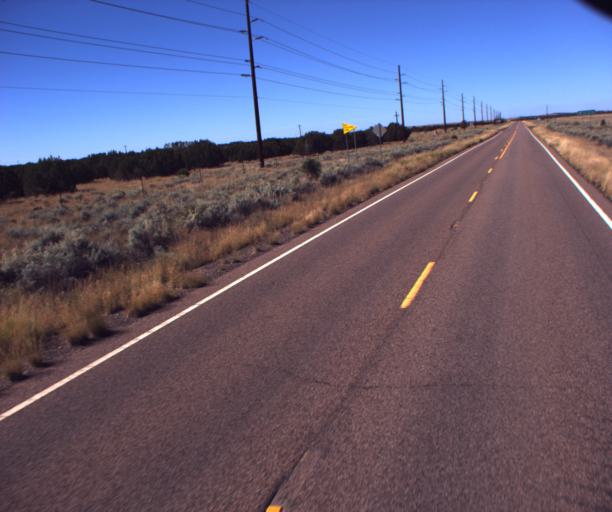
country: US
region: Arizona
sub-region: Navajo County
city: Taylor
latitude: 34.4831
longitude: -110.2773
